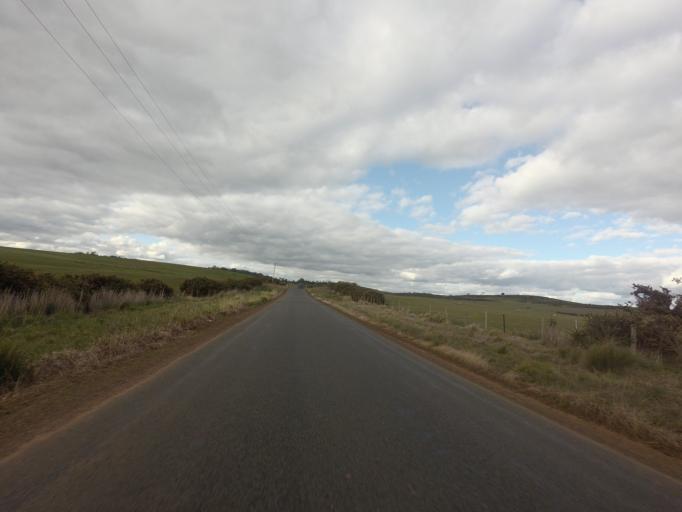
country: AU
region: Tasmania
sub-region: Northern Midlands
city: Evandale
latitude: -41.9048
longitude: 147.3961
